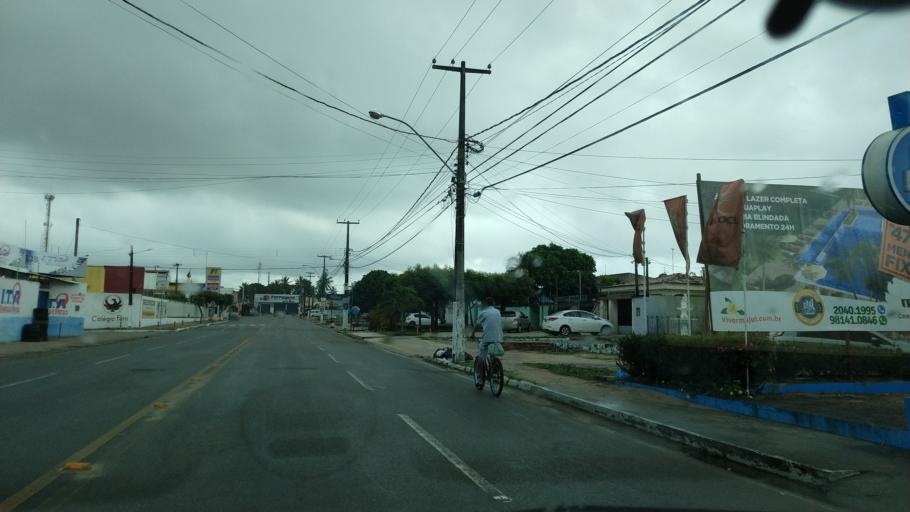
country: BR
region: Rio Grande do Norte
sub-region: Parnamirim
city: Parnamirim
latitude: -5.9274
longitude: -35.2688
